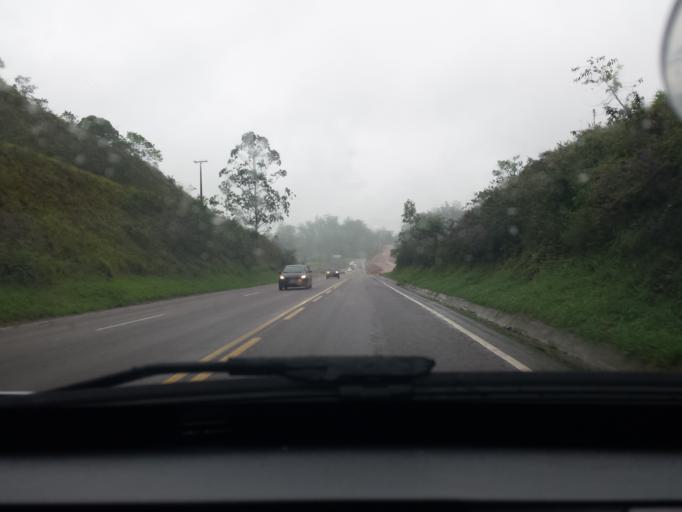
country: BR
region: Santa Catarina
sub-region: Itajai
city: Itajai
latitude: -26.8381
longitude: -48.7763
